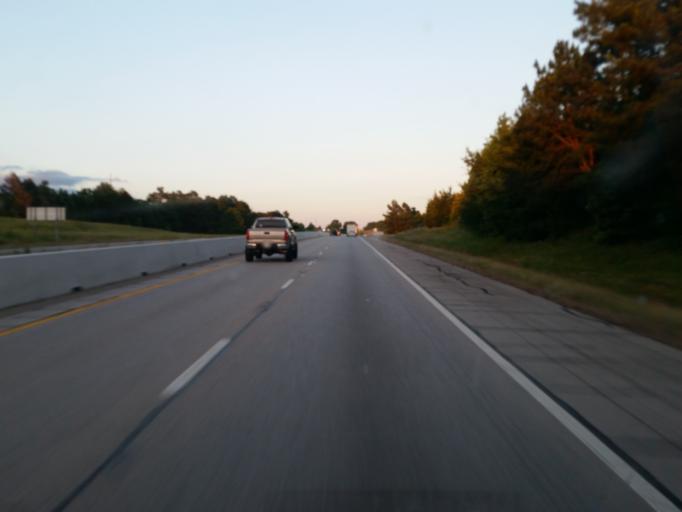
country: US
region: Texas
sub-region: Smith County
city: Hideaway
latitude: 32.4815
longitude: -95.5057
